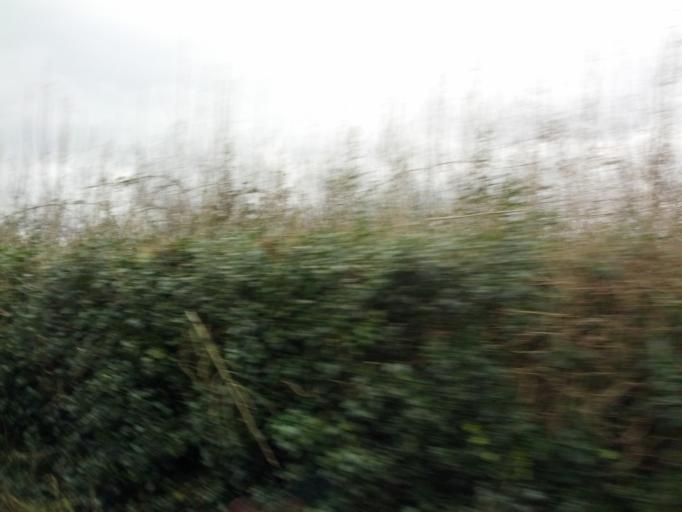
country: IE
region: Connaught
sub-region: County Galway
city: Athenry
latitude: 53.4646
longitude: -8.5759
